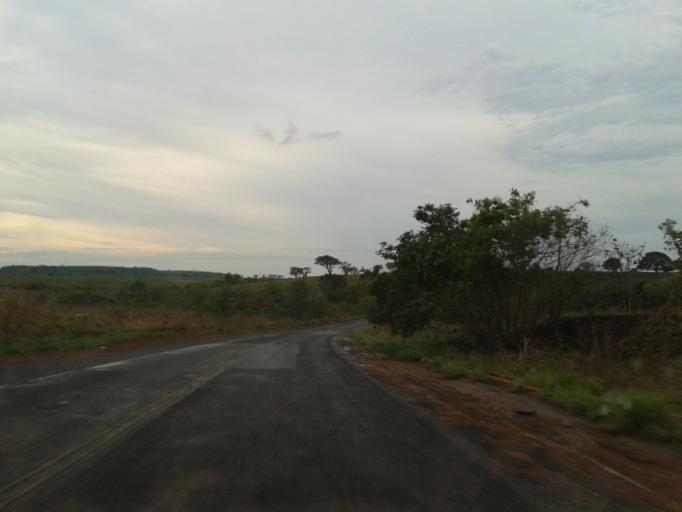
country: BR
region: Goias
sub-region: Quirinopolis
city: Quirinopolis
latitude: -18.1597
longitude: -50.4767
